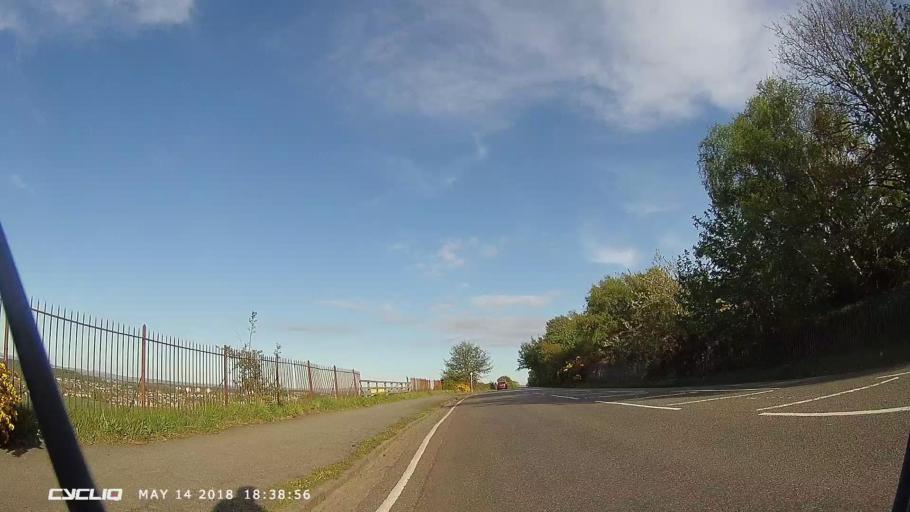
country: GB
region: Scotland
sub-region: Edinburgh
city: Edinburgh
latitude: 55.9157
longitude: -3.1830
